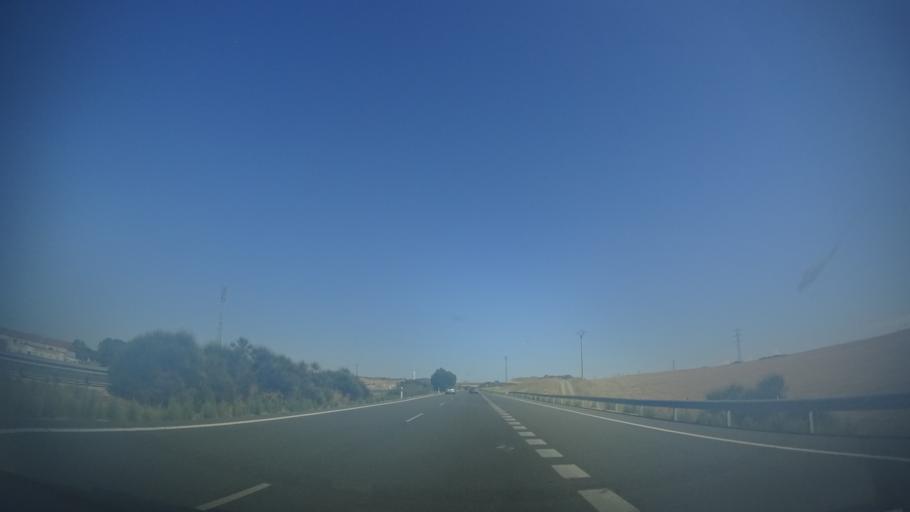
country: ES
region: Castille and Leon
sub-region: Provincia de Valladolid
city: Mota del Marques
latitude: 41.6280
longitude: -5.1801
